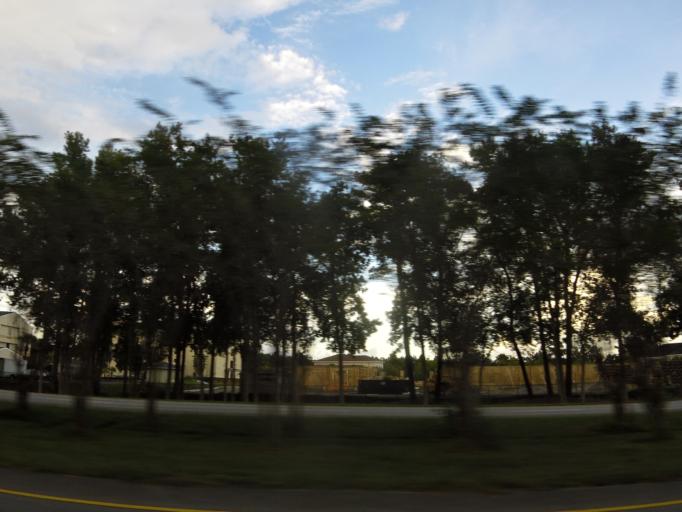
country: US
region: Georgia
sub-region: Glynn County
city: Dock Junction
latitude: 31.2353
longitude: -81.5004
